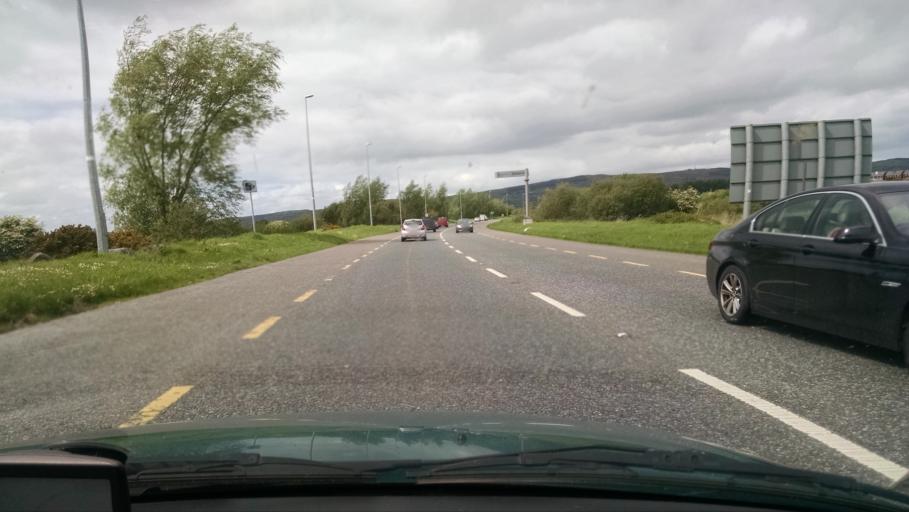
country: IE
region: Munster
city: Moyross
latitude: 52.6667
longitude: -8.6721
